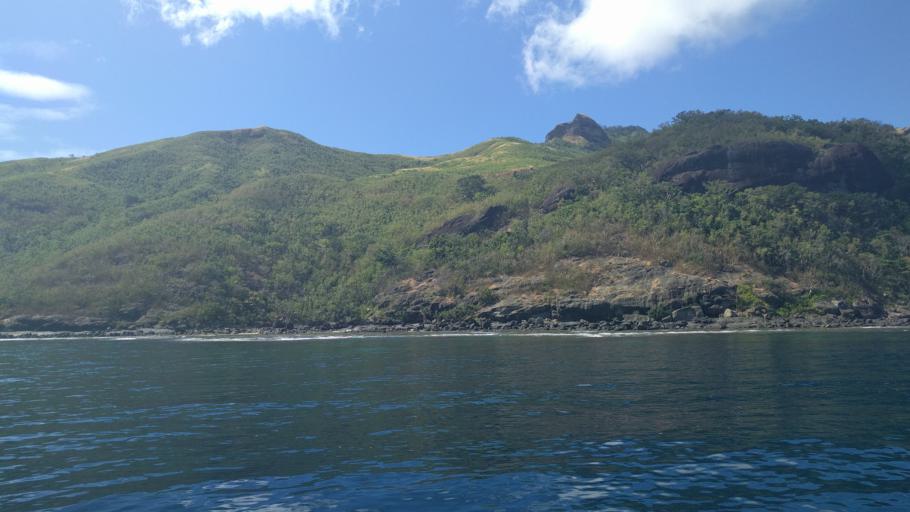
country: FJ
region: Western
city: Lautoka
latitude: -17.2870
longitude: 177.1014
